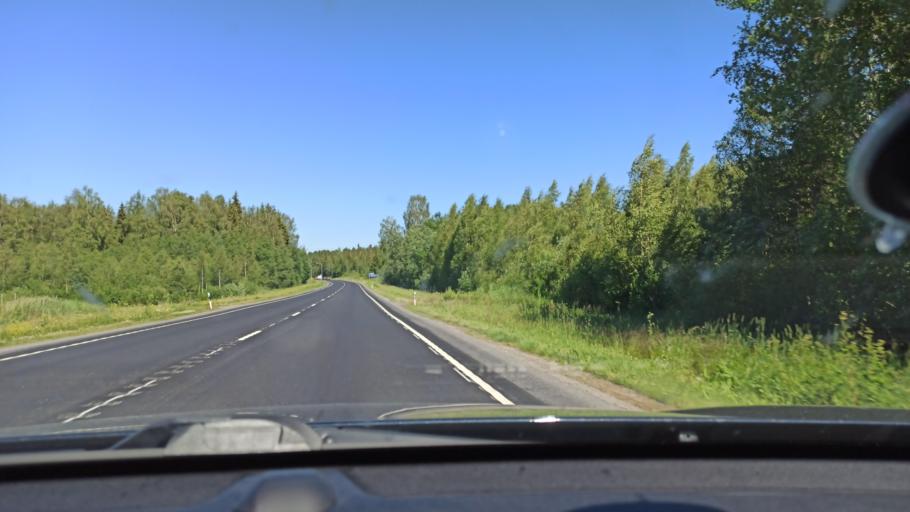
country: FI
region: Ostrobothnia
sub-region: Vaasa
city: Oravais
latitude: 63.2797
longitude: 22.3473
